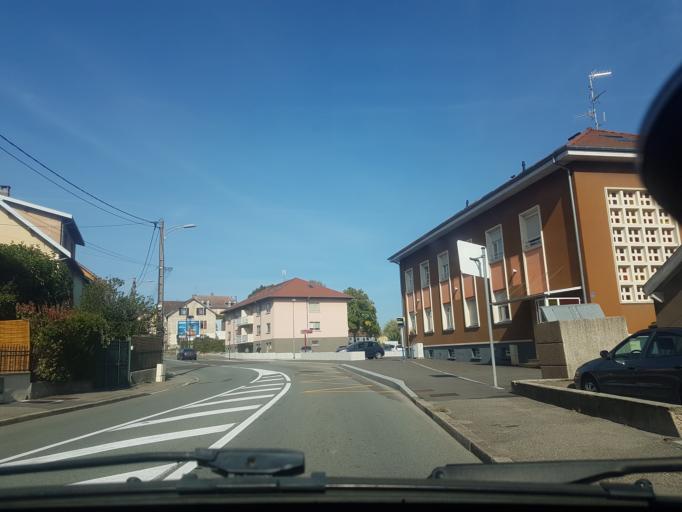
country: FR
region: Franche-Comte
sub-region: Territoire de Belfort
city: Belfort
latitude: 47.6489
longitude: 6.8625
